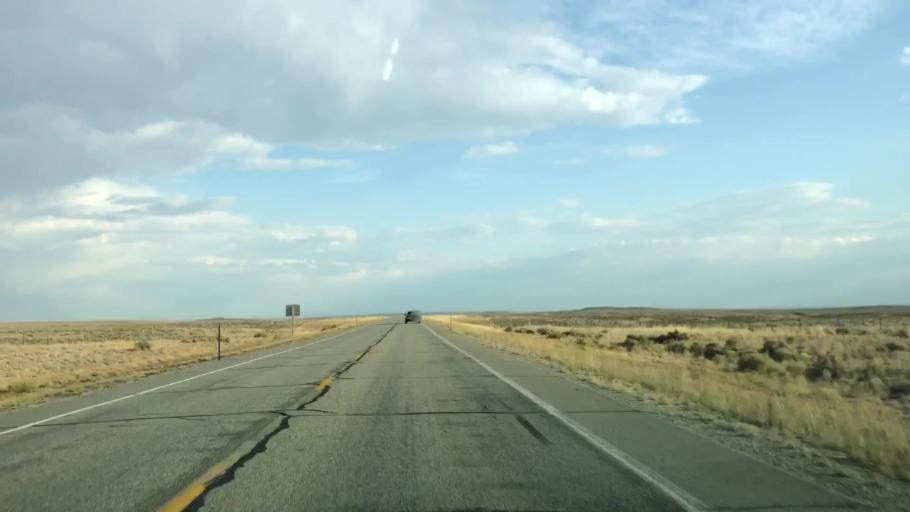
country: US
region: Wyoming
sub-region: Sublette County
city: Pinedale
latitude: 42.3973
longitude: -109.5444
